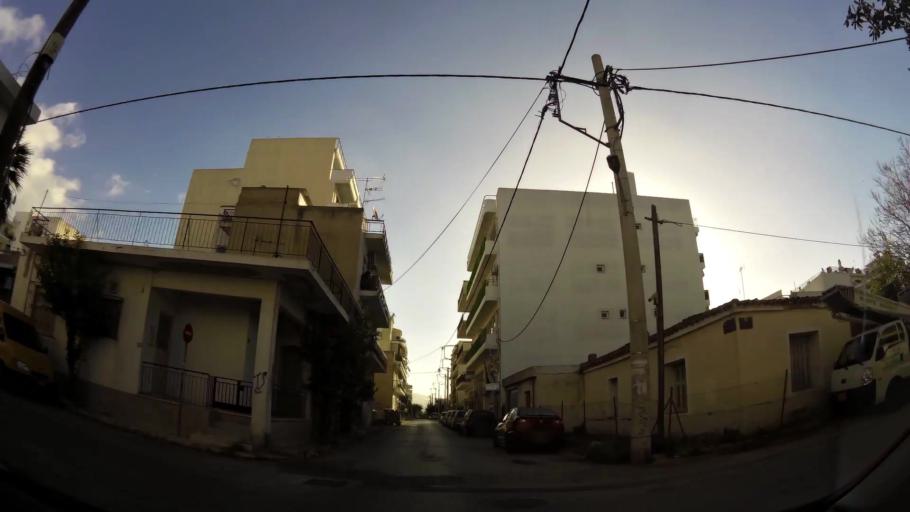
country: GR
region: Attica
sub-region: Nomarchia Anatolikis Attikis
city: Acharnes
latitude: 38.0778
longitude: 23.7411
